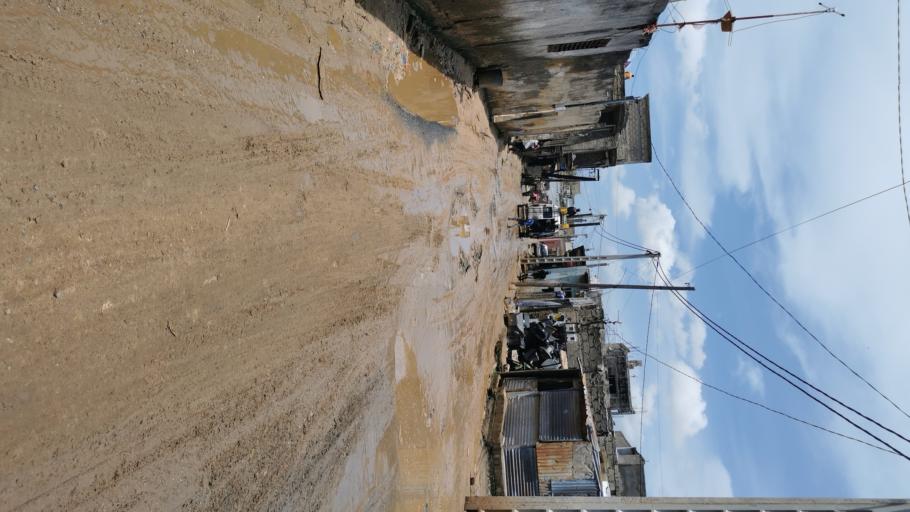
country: SN
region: Dakar
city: Pikine
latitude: 14.7318
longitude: -17.2640
